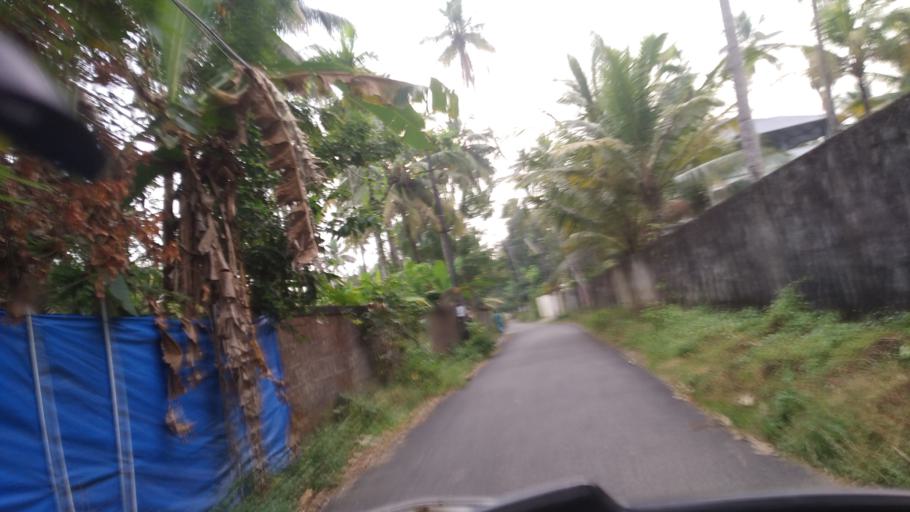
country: IN
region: Kerala
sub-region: Thrissur District
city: Kodungallur
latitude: 10.1376
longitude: 76.2003
